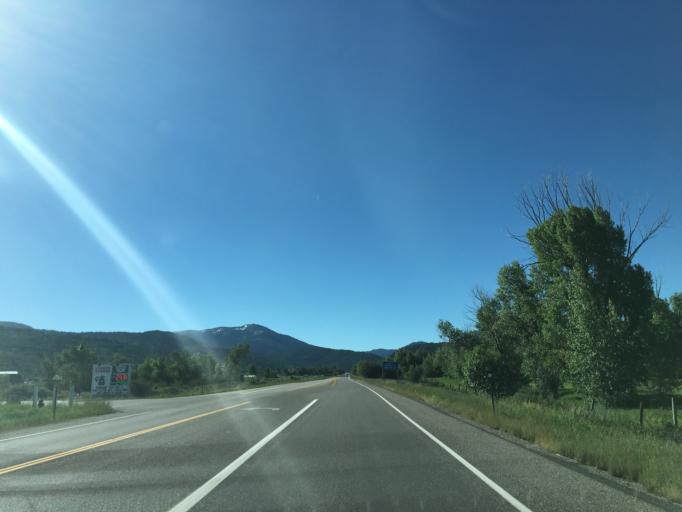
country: US
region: Idaho
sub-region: Teton County
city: Victor
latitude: 43.5947
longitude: -111.1081
